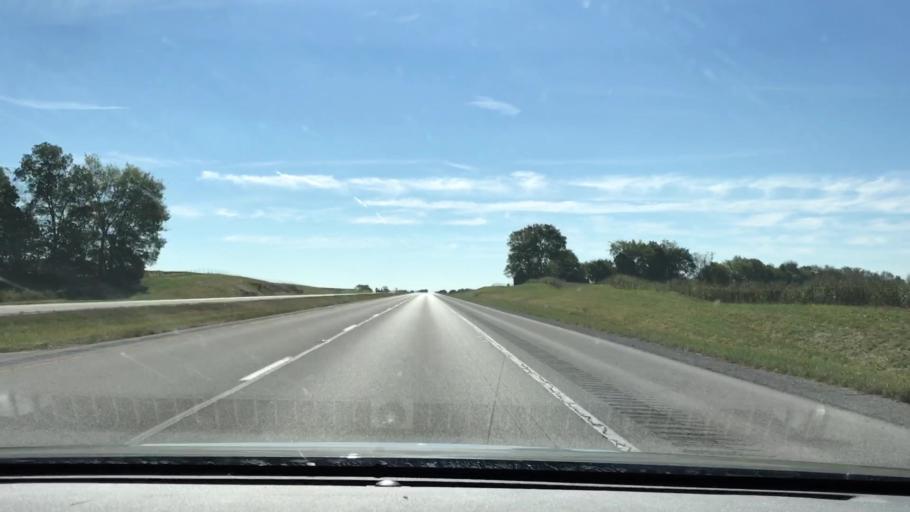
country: US
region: Kentucky
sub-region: Todd County
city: Elkton
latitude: 36.8199
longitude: -87.1445
